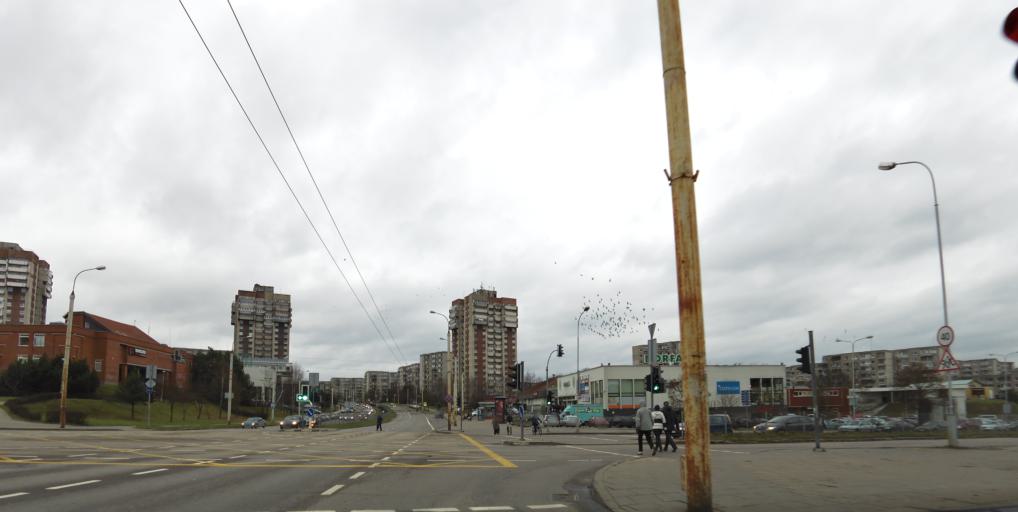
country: LT
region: Vilnius County
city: Justiniskes
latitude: 54.7167
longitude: 25.2214
